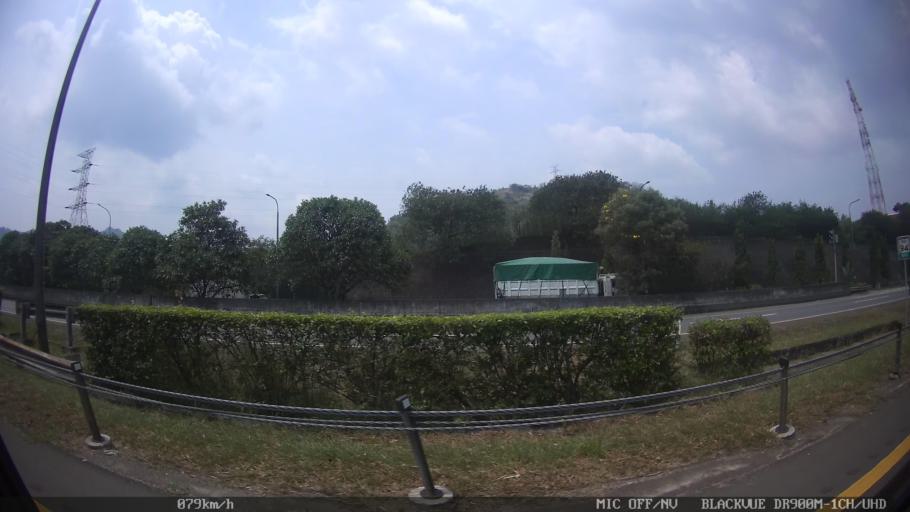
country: ID
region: Banten
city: Curug
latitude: -5.9849
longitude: 106.0340
